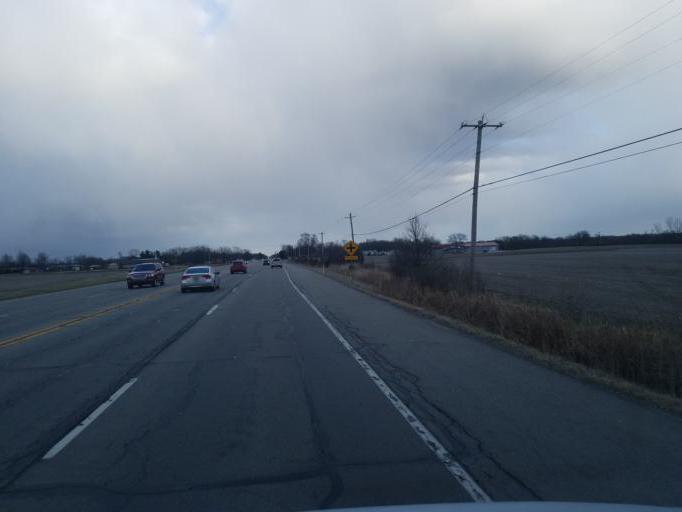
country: US
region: Indiana
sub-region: Hancock County
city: New Palestine
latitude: 39.7801
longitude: -85.8817
